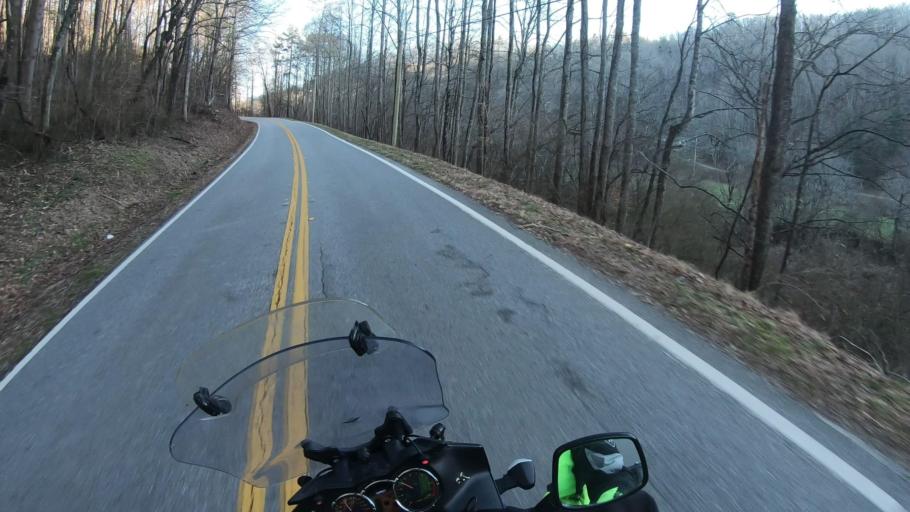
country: US
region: Georgia
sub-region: Union County
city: Blairsville
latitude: 34.7233
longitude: -84.0787
